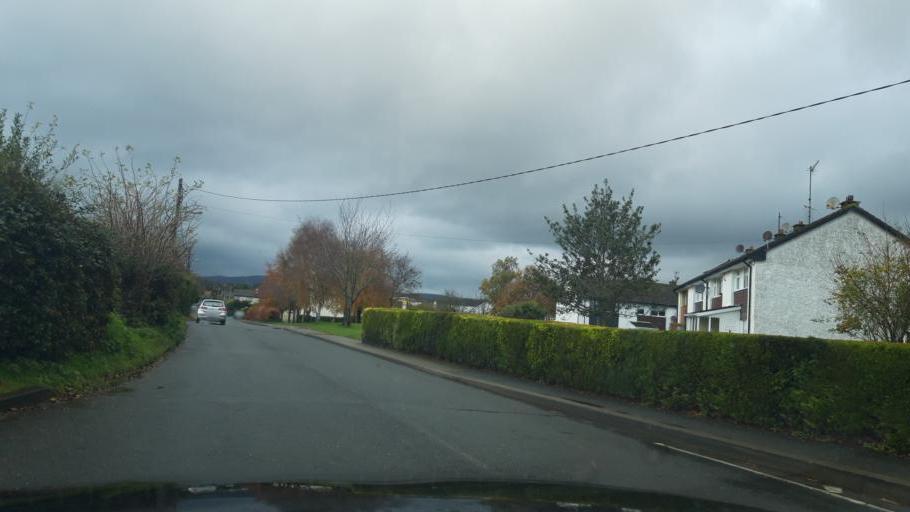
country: IE
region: Leinster
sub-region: Wicklow
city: Kilcoole
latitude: 53.1047
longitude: -6.0646
